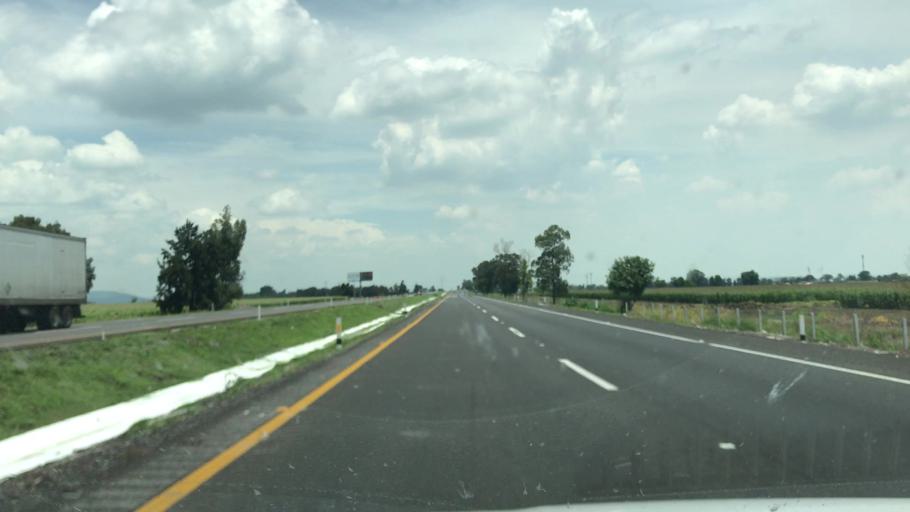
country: MX
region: Guanajuato
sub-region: Salamanca
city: San Vicente de Flores
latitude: 20.6343
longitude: -101.2559
